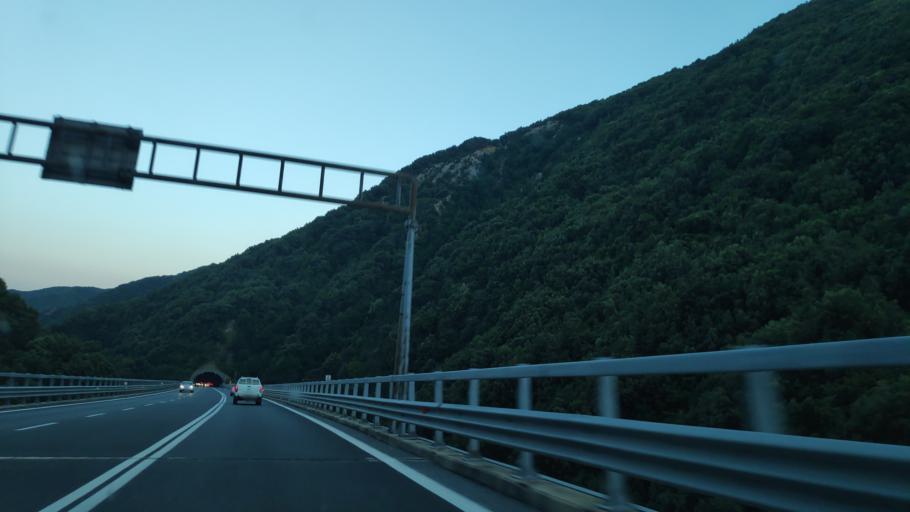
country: IT
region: Calabria
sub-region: Provincia di Reggio Calabria
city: Amato
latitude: 38.3682
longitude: 16.1836
